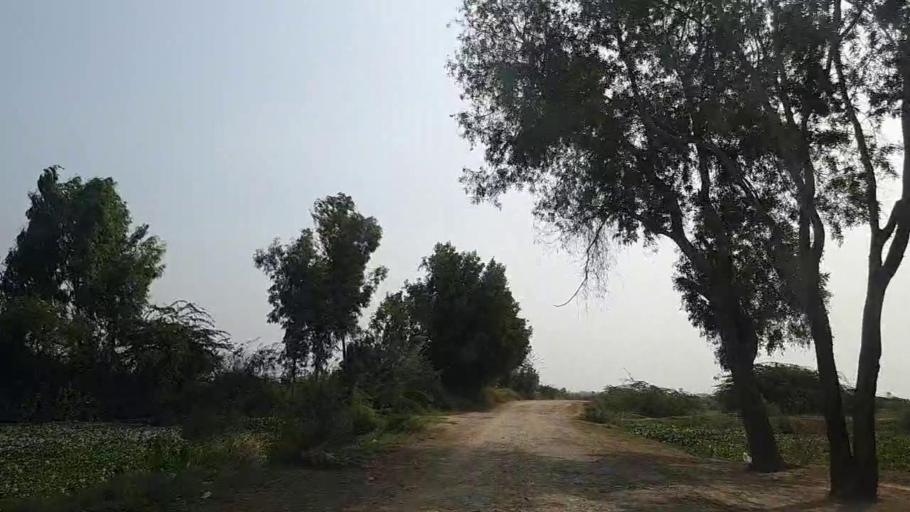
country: PK
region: Sindh
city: Mirpur Sakro
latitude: 24.5919
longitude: 67.7187
